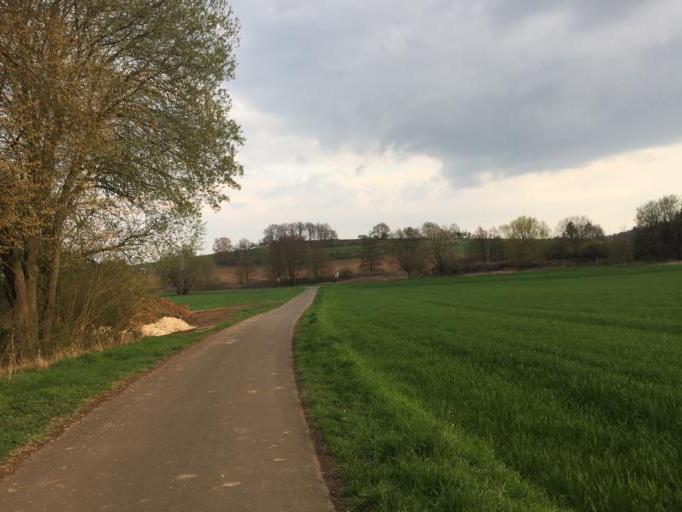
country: DE
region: Hesse
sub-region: Regierungsbezirk Giessen
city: Laubach
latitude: 50.5410
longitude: 8.9652
